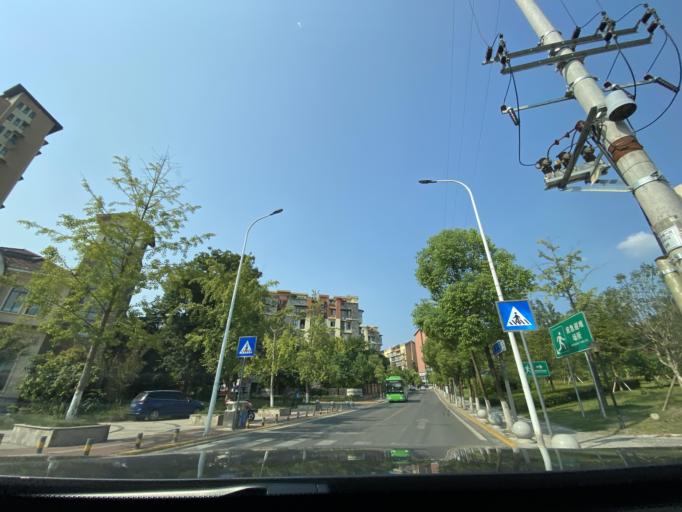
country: CN
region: Sichuan
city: Jiancheng
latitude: 30.4163
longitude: 104.5431
